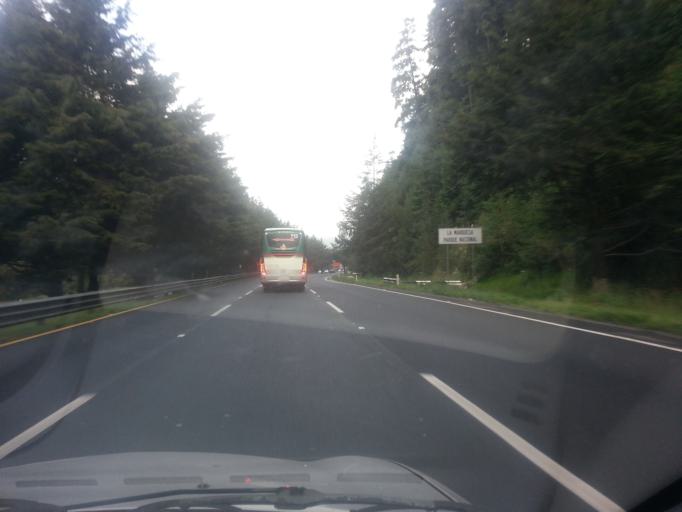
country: MX
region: Mexico City
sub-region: Cuajimalpa de Morelos
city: San Lorenzo Acopilco
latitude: 19.2988
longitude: -99.3608
